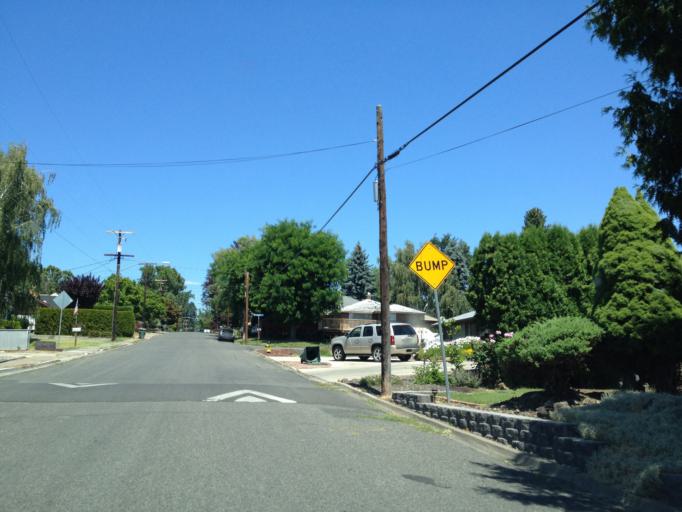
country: US
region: Washington
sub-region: Yakima County
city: West Valley
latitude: 46.5939
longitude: -120.5566
